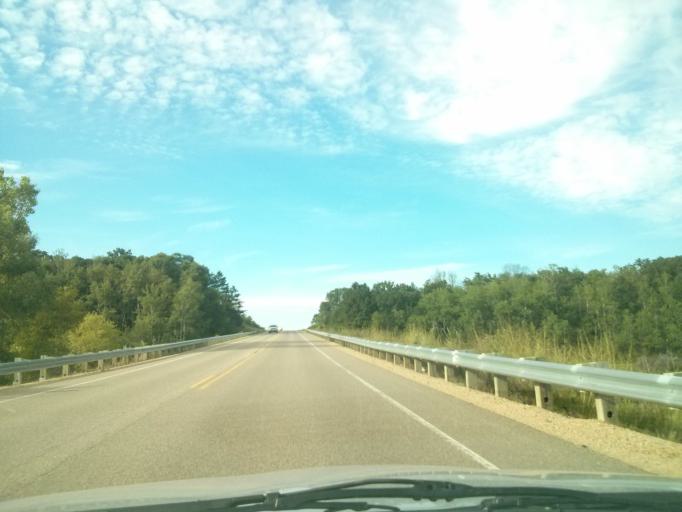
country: US
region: Minnesota
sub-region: Washington County
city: Afton
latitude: 44.8703
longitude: -92.7310
